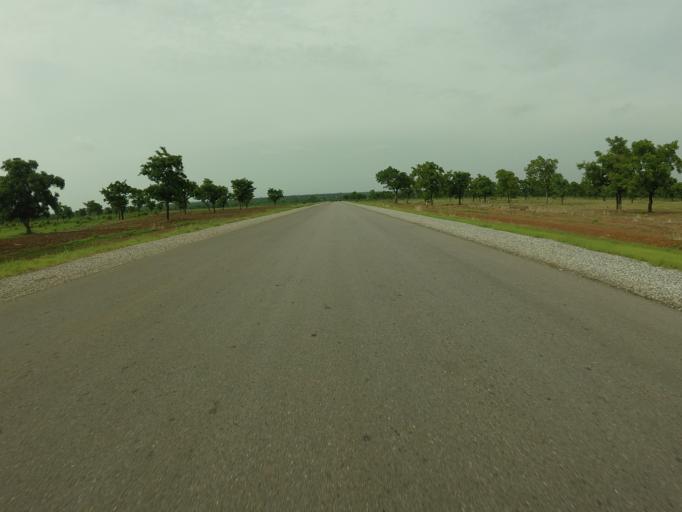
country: GH
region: Northern
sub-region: Yendi
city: Yendi
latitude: 9.8052
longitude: -0.1133
